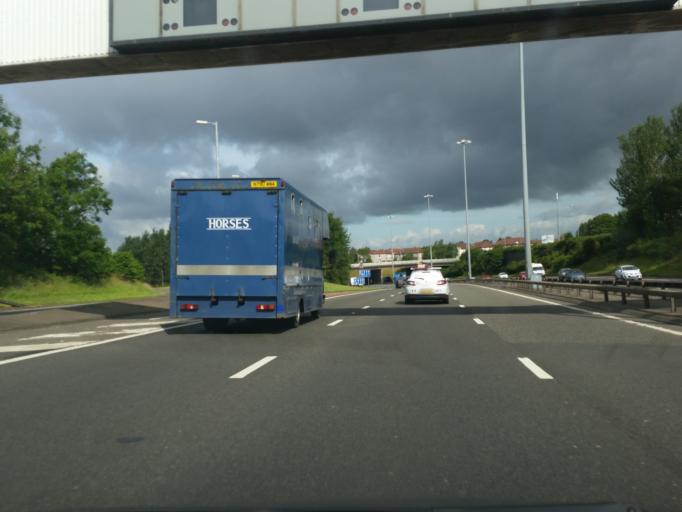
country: GB
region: Scotland
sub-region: North Lanarkshire
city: Stepps
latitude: 55.8721
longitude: -4.1808
